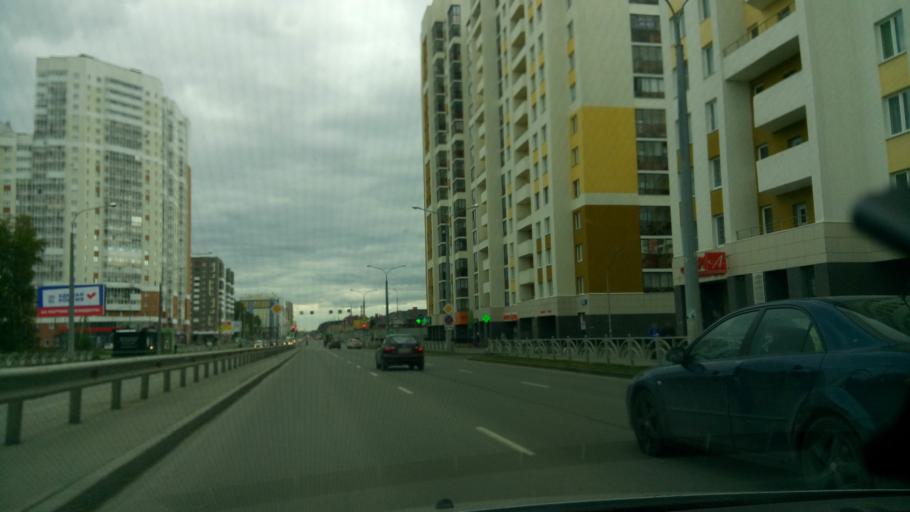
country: RU
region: Sverdlovsk
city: Sovkhoznyy
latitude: 56.7894
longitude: 60.5281
